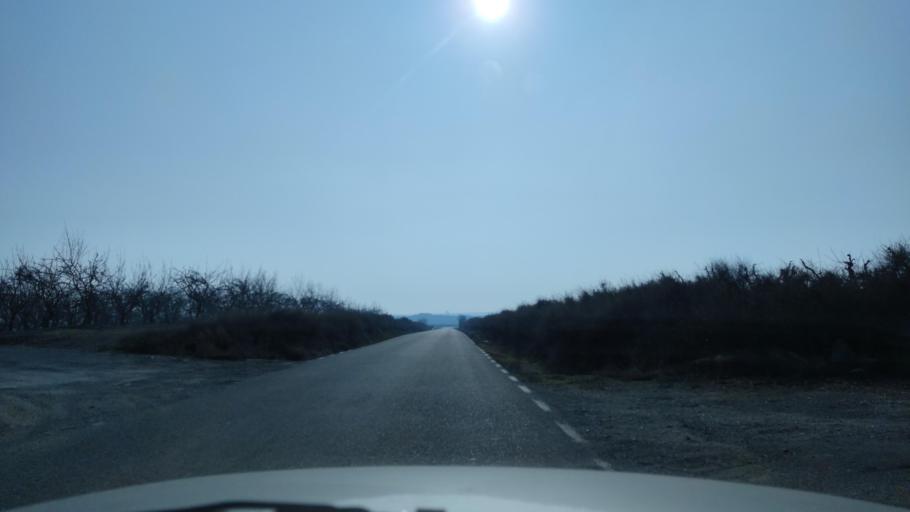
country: ES
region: Catalonia
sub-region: Provincia de Lleida
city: Sunyer
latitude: 41.5393
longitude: 0.5767
